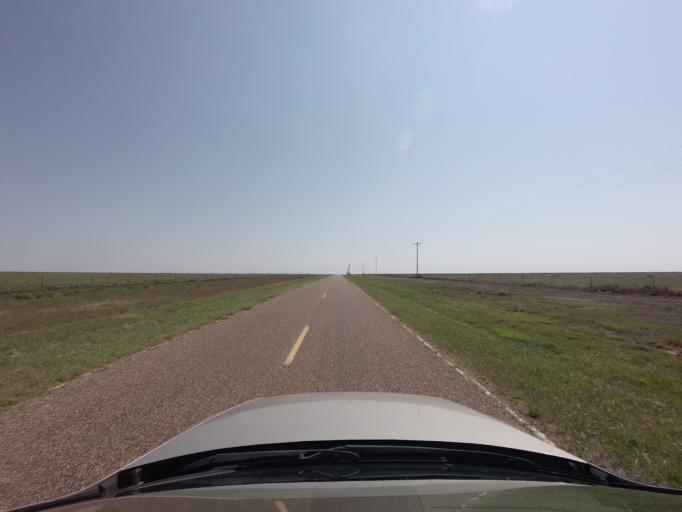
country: US
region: New Mexico
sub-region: Curry County
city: Cannon Air Force Base
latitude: 34.6331
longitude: -103.3753
